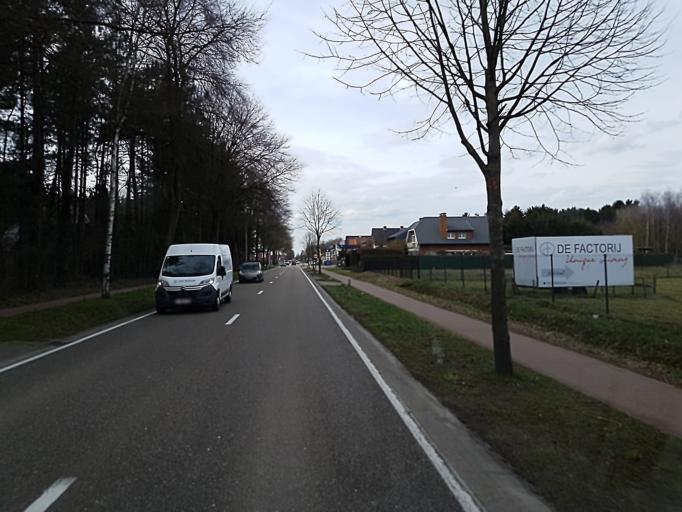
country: BE
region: Flanders
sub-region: Provincie Antwerpen
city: Retie
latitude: 51.2767
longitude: 5.0673
